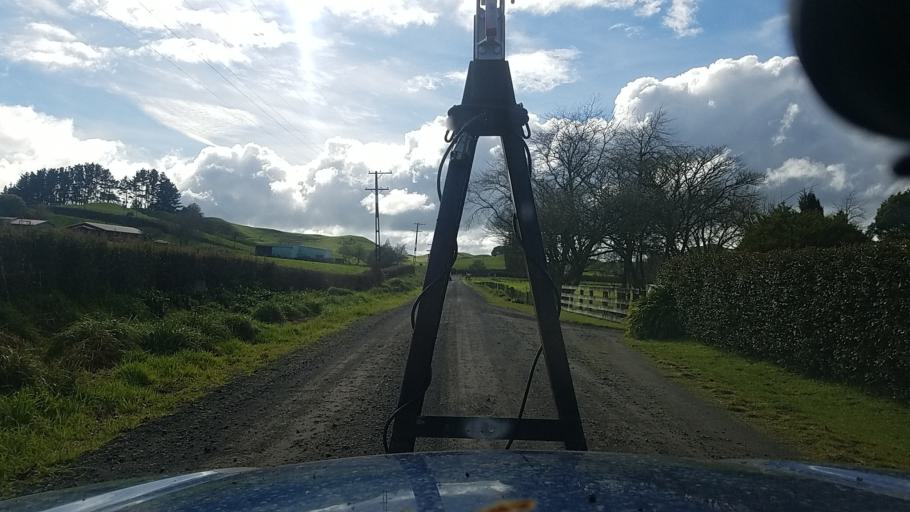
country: NZ
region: Taranaki
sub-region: South Taranaki District
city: Eltham
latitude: -39.3432
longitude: 174.4204
